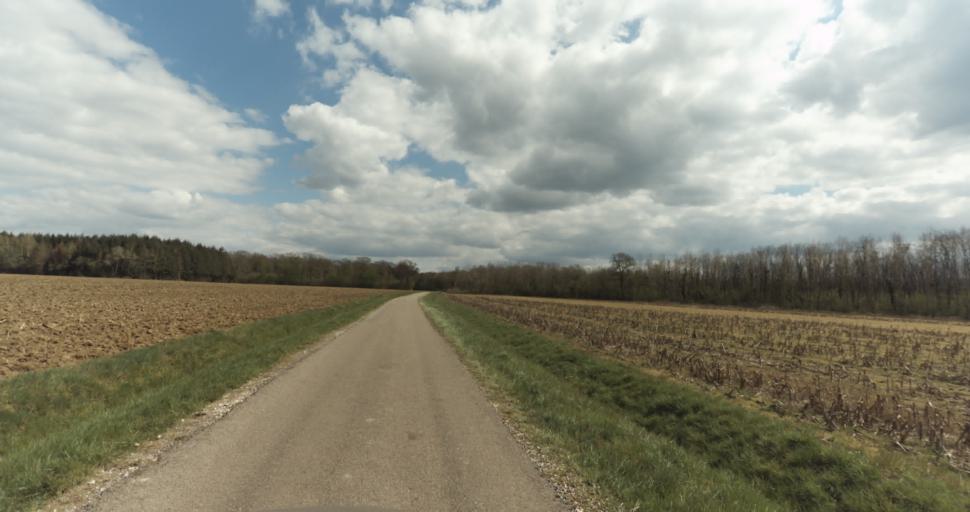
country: FR
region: Bourgogne
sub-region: Departement de la Cote-d'Or
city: Auxonne
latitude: 47.1727
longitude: 5.4188
